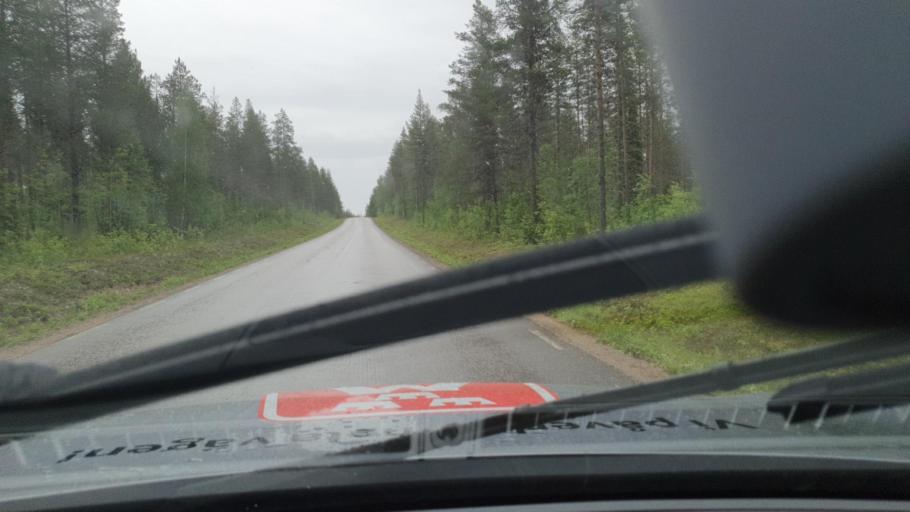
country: SE
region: Norrbotten
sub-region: Pajala Kommun
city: Pajala
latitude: 66.8324
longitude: 23.1104
